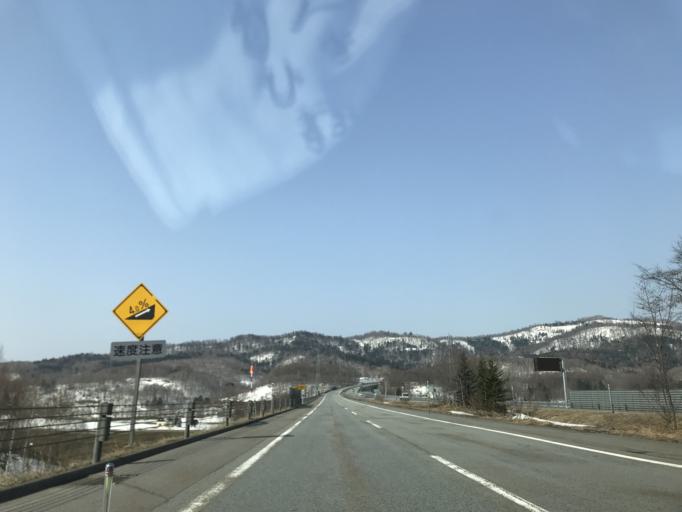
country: JP
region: Hokkaido
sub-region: Asahikawa-shi
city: Asahikawa
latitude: 43.7950
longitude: 142.2864
